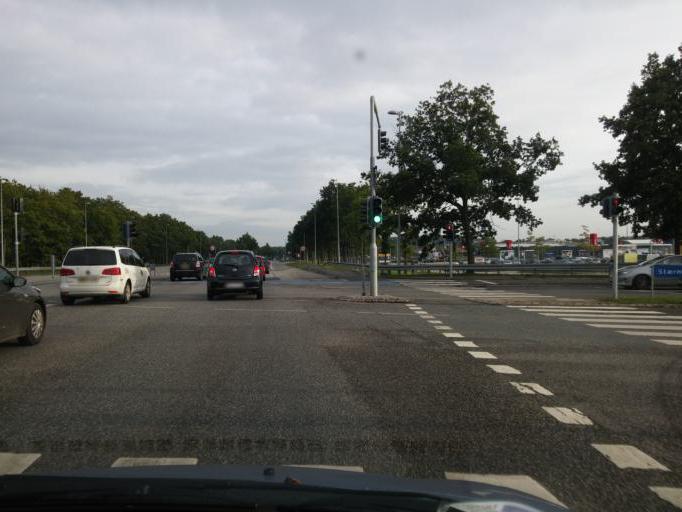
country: DK
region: South Denmark
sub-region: Odense Kommune
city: Neder Holluf
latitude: 55.3821
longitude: 10.4315
